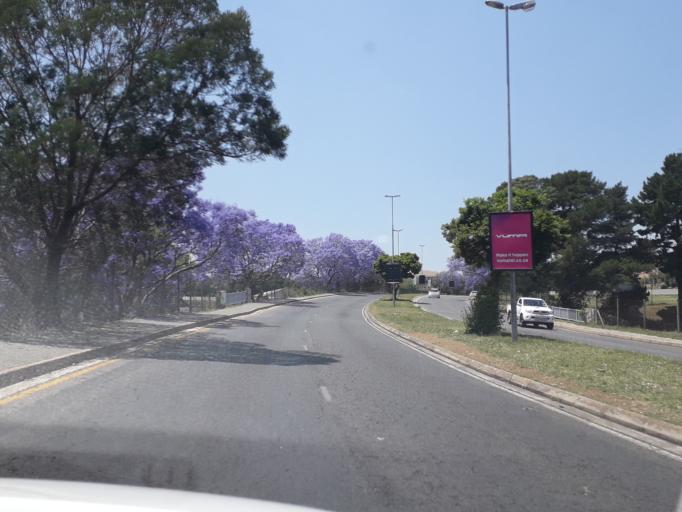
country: ZA
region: Gauteng
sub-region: City of Johannesburg Metropolitan Municipality
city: Johannesburg
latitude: -26.0978
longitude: 27.9817
